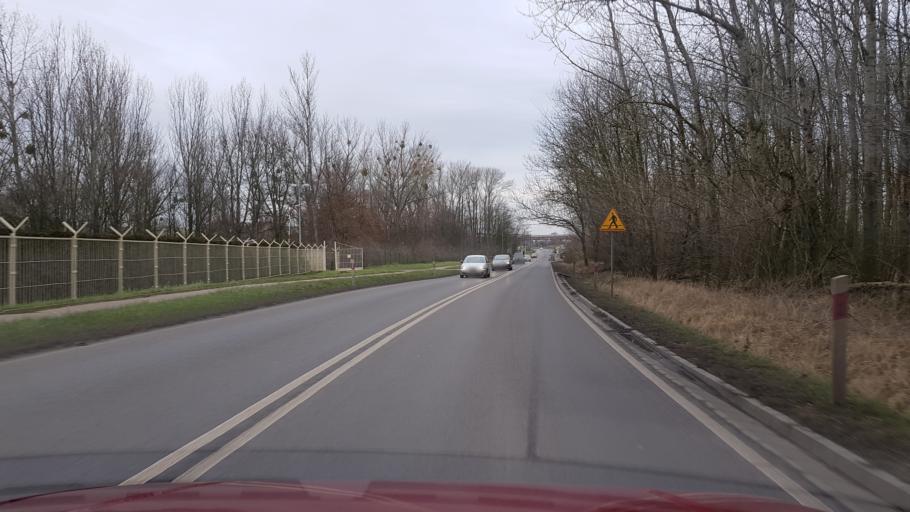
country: PL
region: West Pomeranian Voivodeship
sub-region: Powiat policki
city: Police
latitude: 53.5680
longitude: 14.5574
